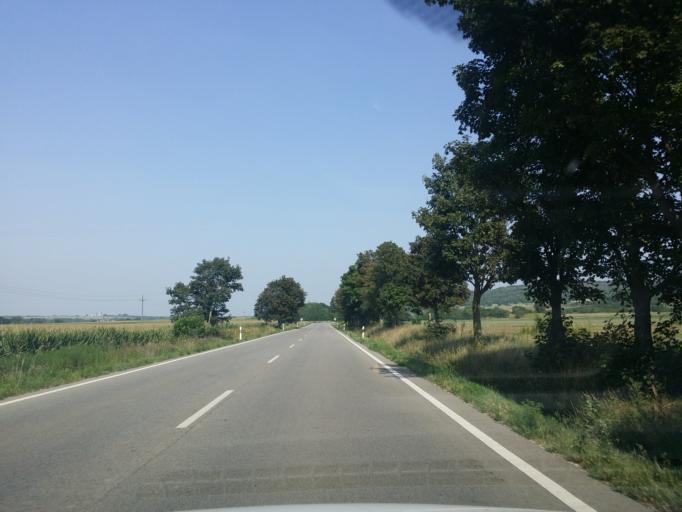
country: HU
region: Tolna
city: Simontornya
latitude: 46.7358
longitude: 18.5063
